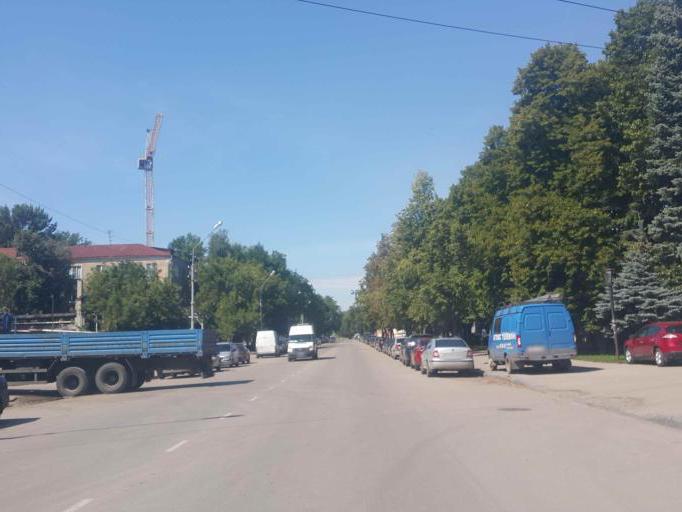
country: RU
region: Tambov
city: Tambov
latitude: 52.7214
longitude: 41.4361
